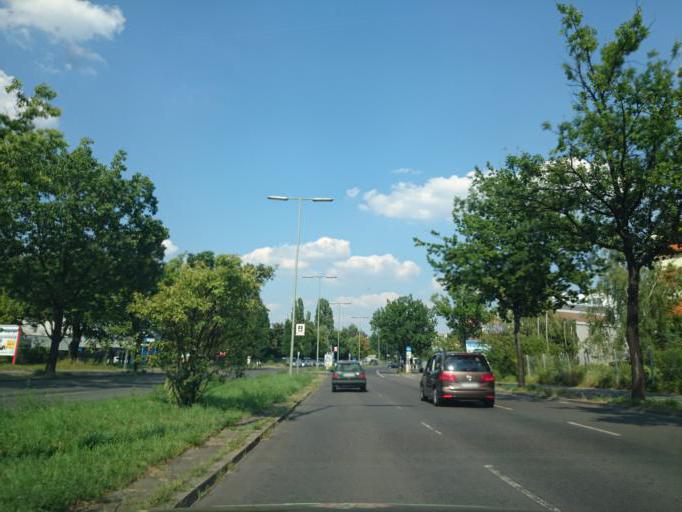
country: DE
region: Berlin
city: Marienfelde
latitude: 52.4102
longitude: 13.3796
